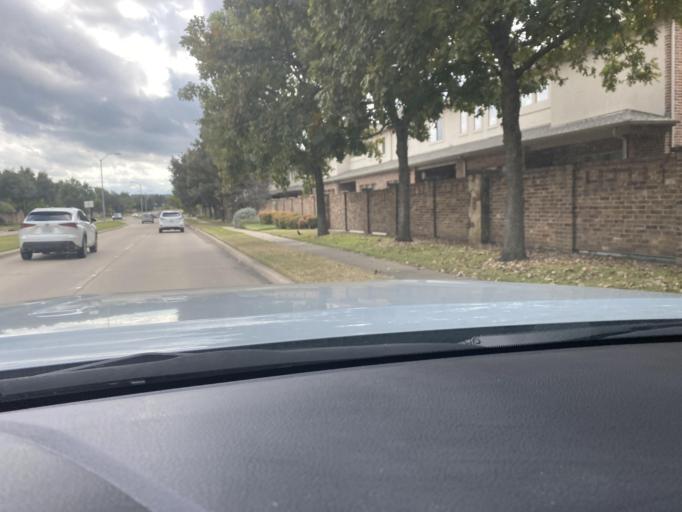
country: US
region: Texas
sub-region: Dallas County
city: Addison
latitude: 33.0409
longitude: -96.7895
